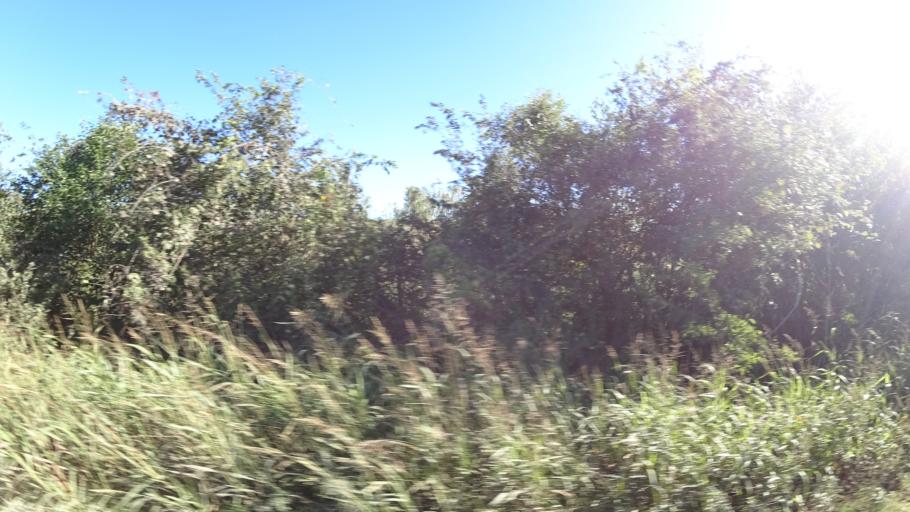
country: US
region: Texas
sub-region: Travis County
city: Austin
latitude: 30.2433
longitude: -97.6690
